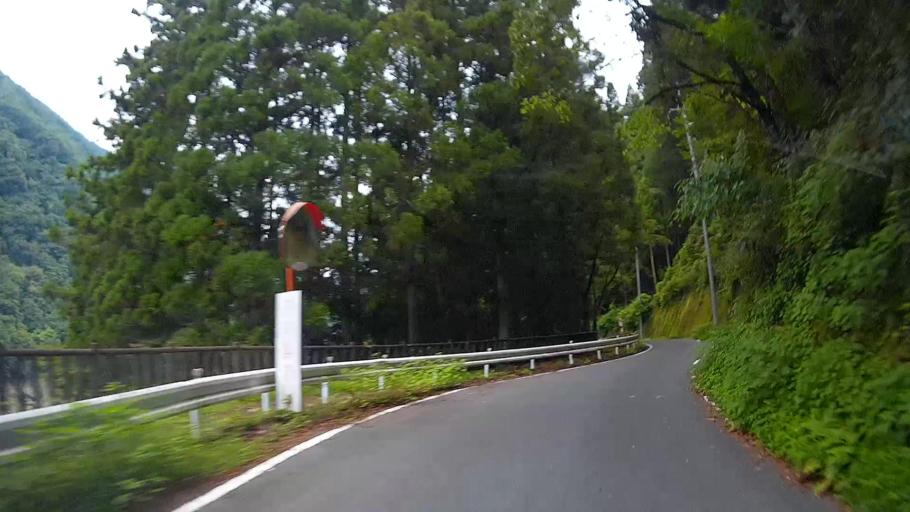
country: JP
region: Saitama
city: Chichibu
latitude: 35.9421
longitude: 138.9031
